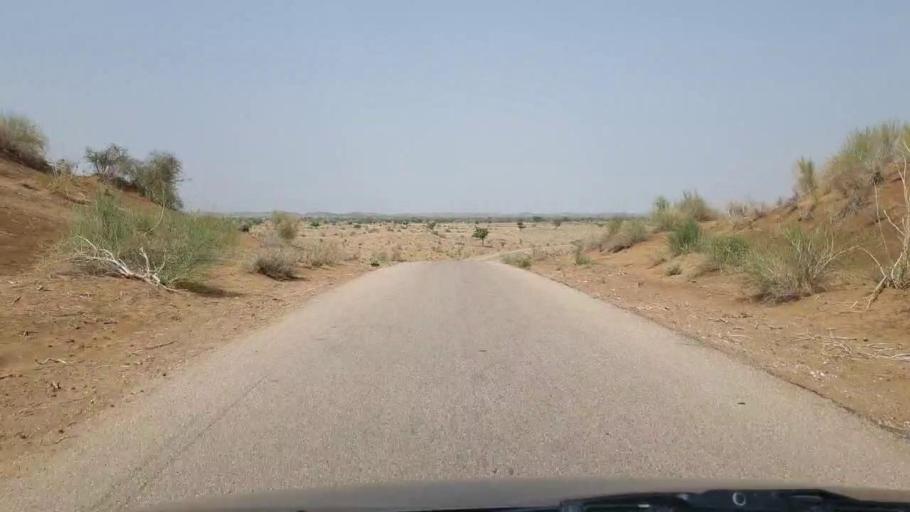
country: PK
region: Sindh
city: Chor
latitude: 25.4732
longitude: 70.5043
